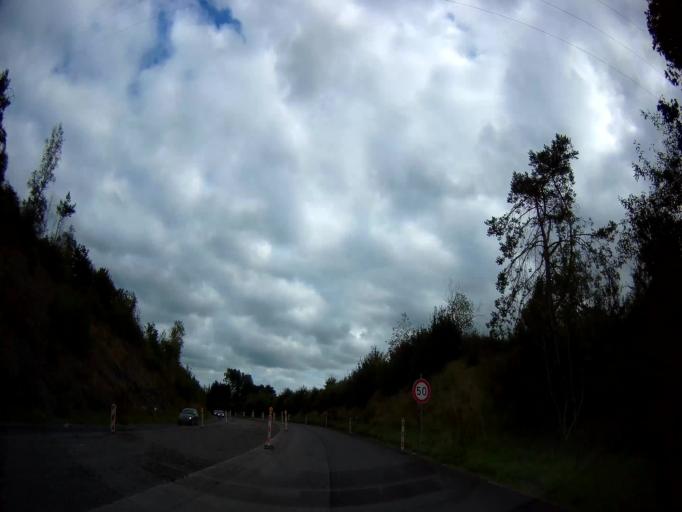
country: BE
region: Wallonia
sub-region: Province du Luxembourg
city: Tenneville
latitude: 50.0804
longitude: 5.5343
